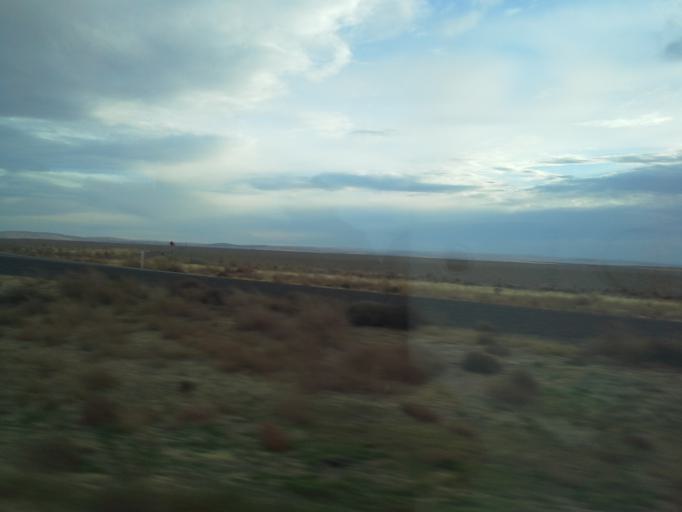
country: US
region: Oregon
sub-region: Umatilla County
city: Stanfield
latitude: 45.7192
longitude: -119.0166
